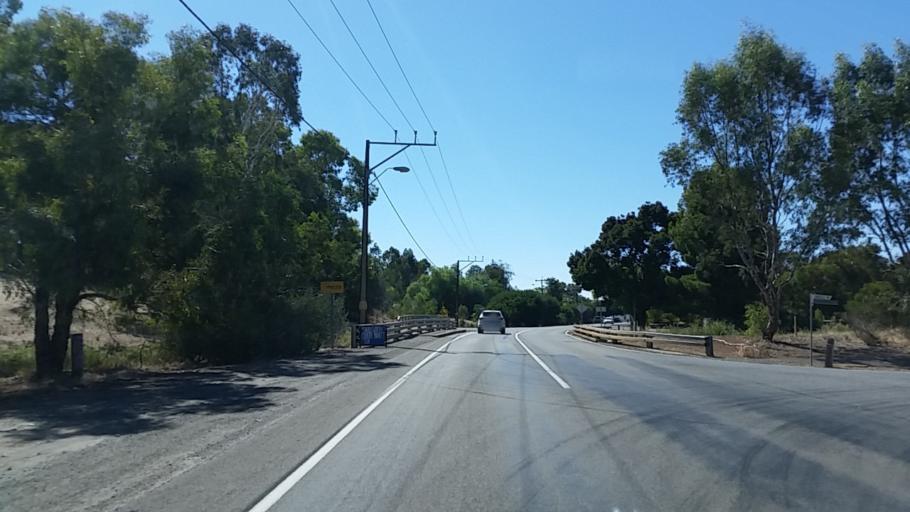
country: AU
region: South Australia
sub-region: Light
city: Kapunda
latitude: -34.0812
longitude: 138.7807
